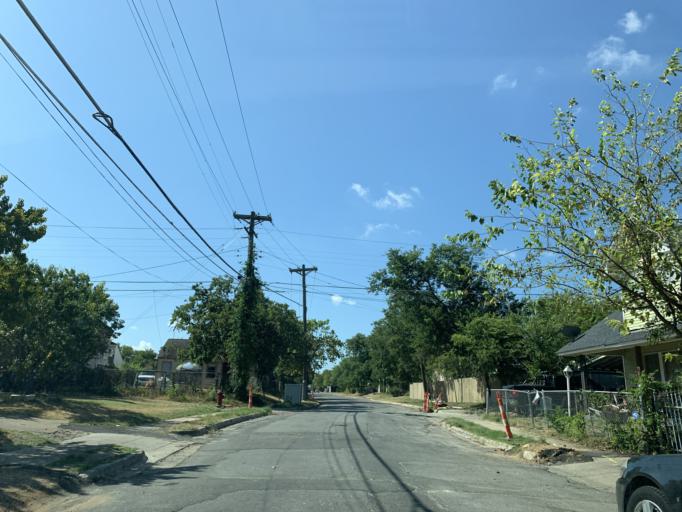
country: US
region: Texas
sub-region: Dallas County
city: Cockrell Hill
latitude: 32.7370
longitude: -96.8716
